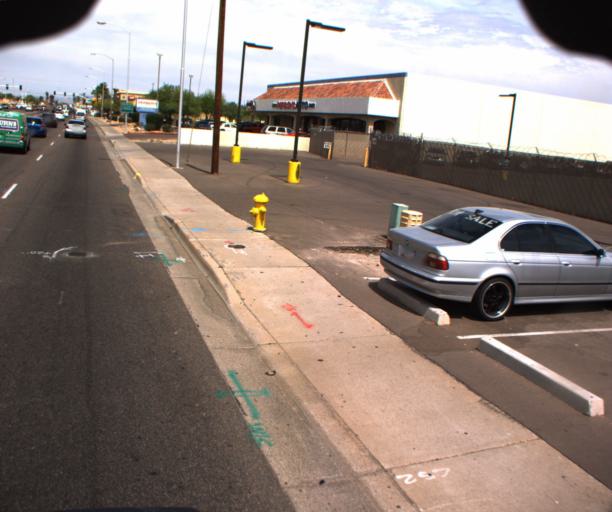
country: US
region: Arizona
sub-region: Maricopa County
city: Mesa
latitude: 33.3914
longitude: -111.8400
